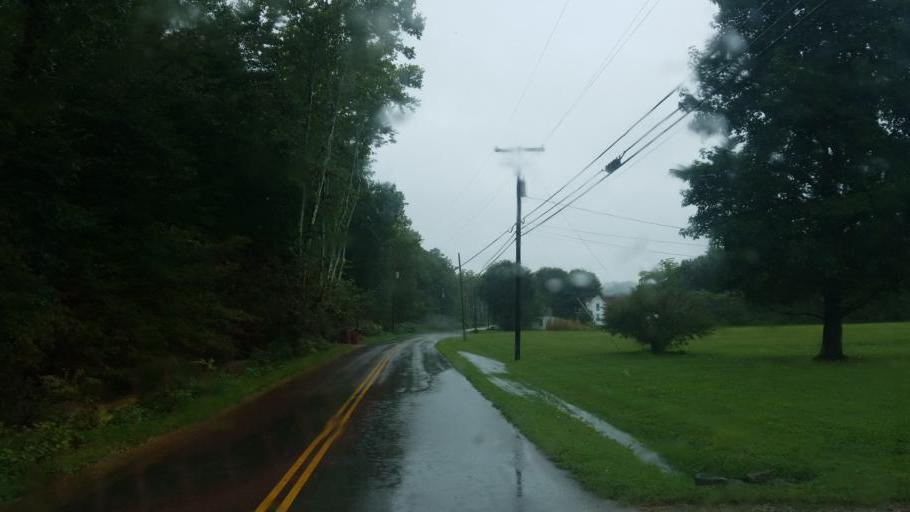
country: US
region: Ohio
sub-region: Scioto County
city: West Portsmouth
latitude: 38.7317
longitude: -83.0592
